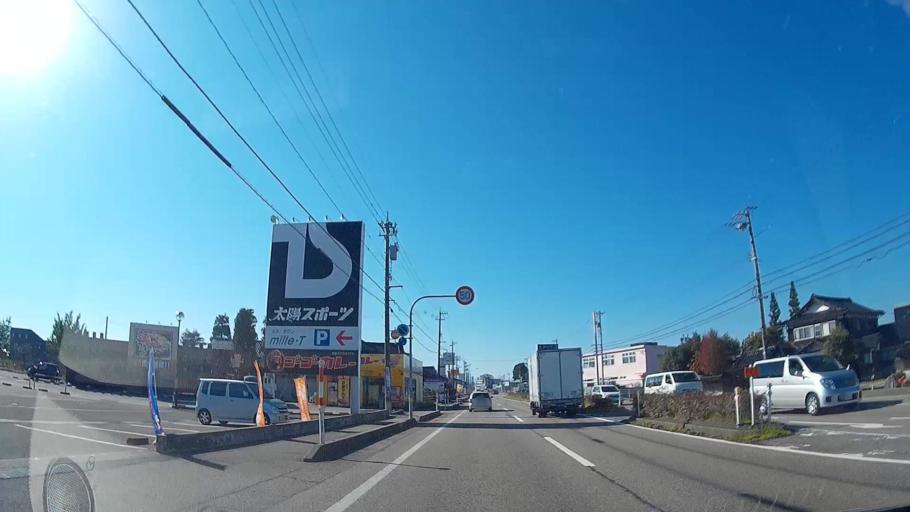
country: JP
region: Toyama
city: Takaoka
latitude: 36.6591
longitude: 136.9705
